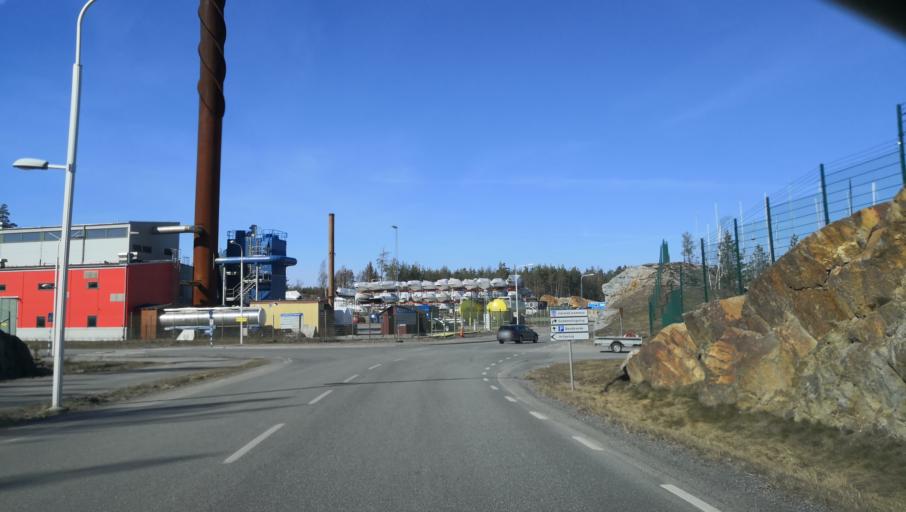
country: SE
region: Stockholm
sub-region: Varmdo Kommun
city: Gustavsberg
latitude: 59.3123
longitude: 18.3788
